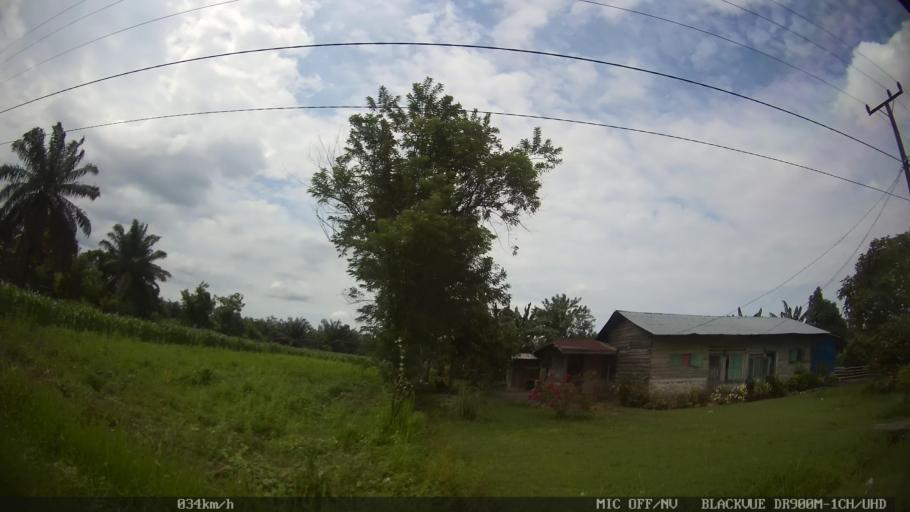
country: ID
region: North Sumatra
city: Sunggal
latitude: 3.6361
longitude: 98.5985
